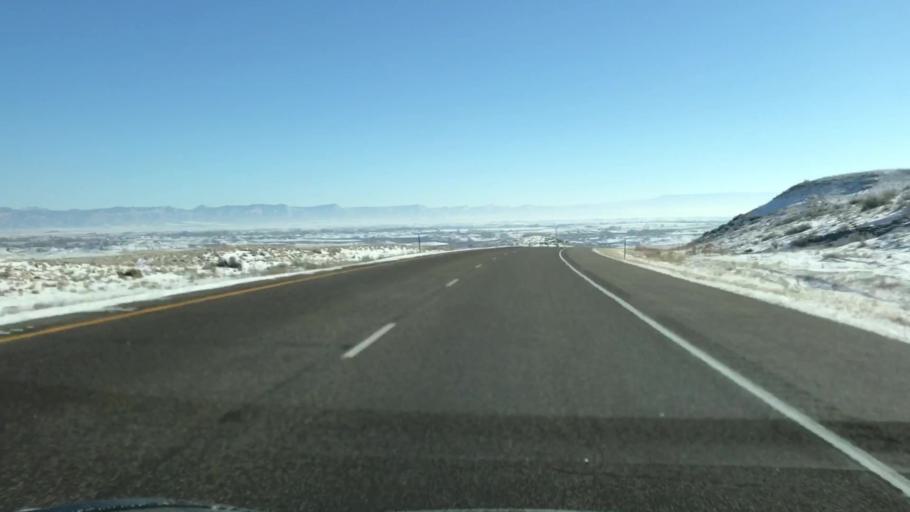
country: US
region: Colorado
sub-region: Mesa County
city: Loma
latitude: 39.2299
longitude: -108.9087
